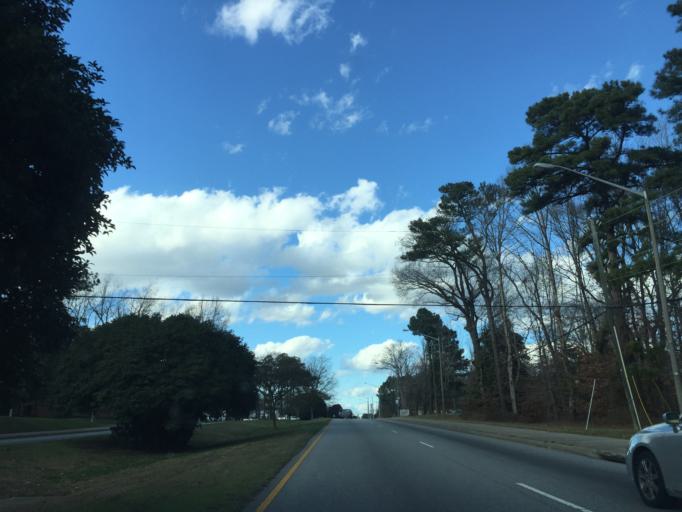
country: US
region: Virginia
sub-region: York County
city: Yorktown
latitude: 37.1069
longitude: -76.5139
